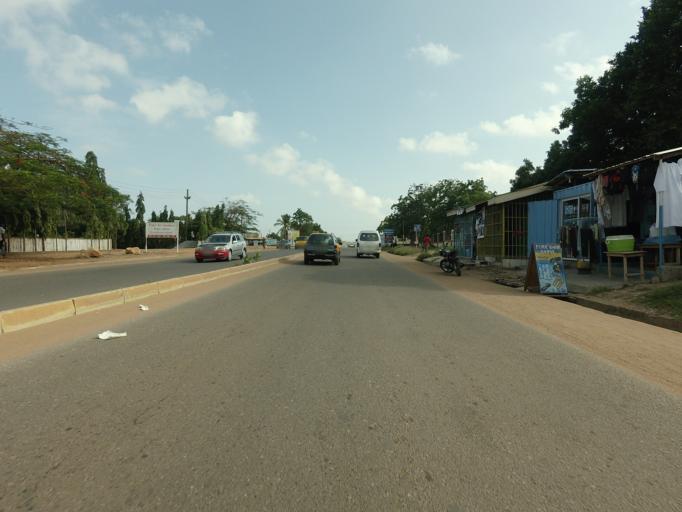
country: GH
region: Greater Accra
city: Tema
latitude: 5.6616
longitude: -0.0509
